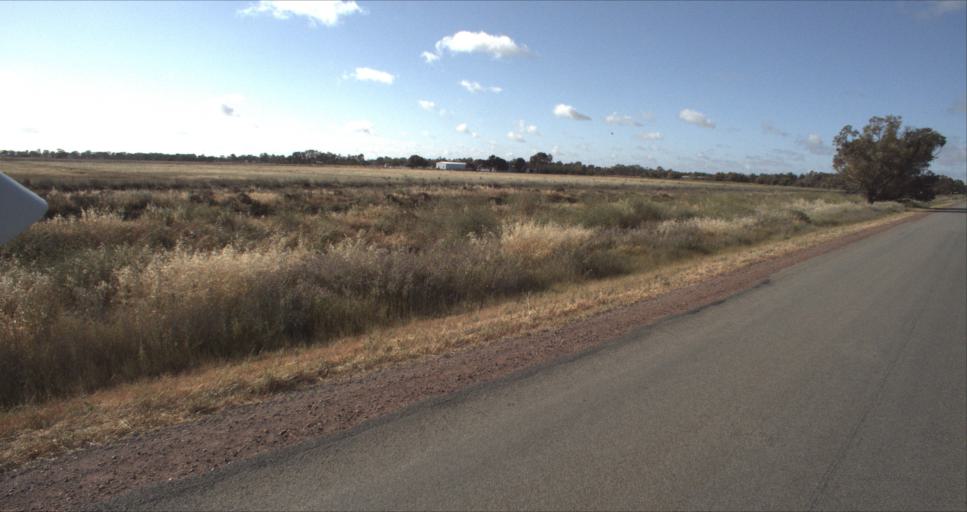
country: AU
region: New South Wales
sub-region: Leeton
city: Leeton
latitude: -34.5224
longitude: 146.3903
